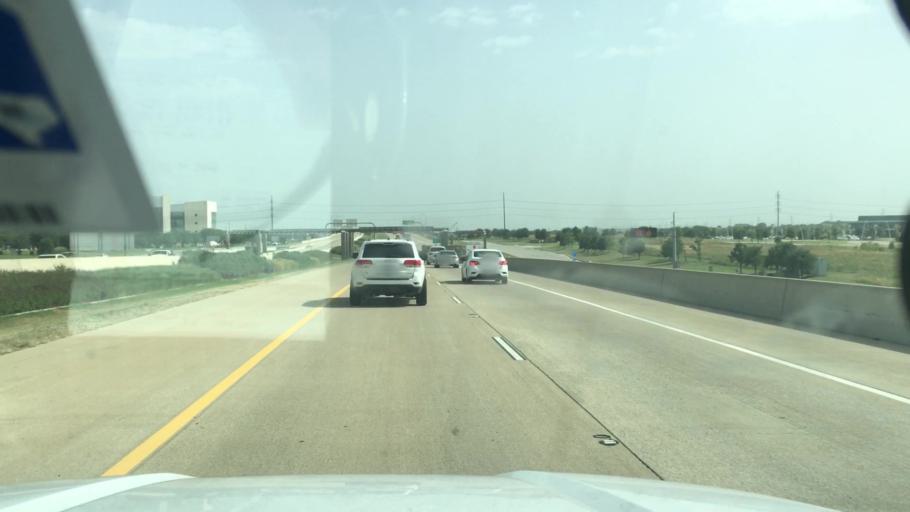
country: US
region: Texas
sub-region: Dallas County
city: Grand Prairie
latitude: 32.7047
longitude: -97.0248
